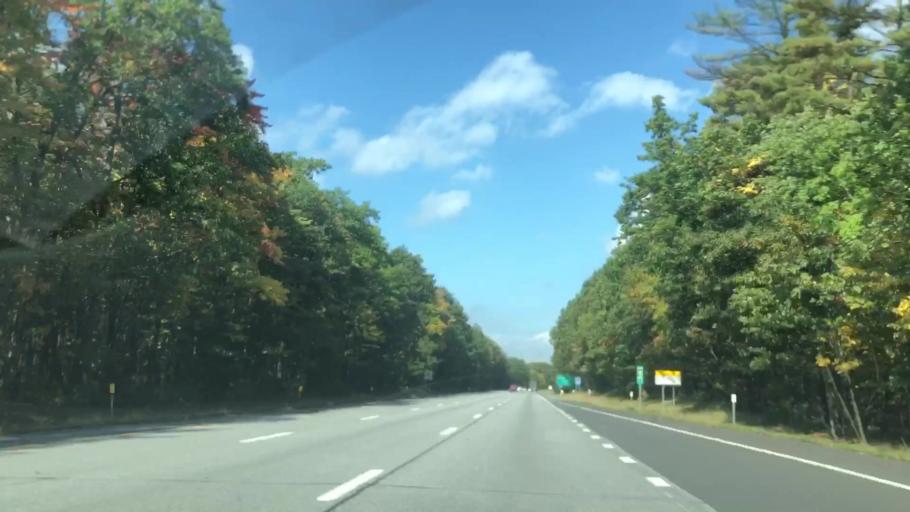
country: US
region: New York
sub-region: Warren County
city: West Glens Falls
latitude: 43.2782
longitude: -73.6777
